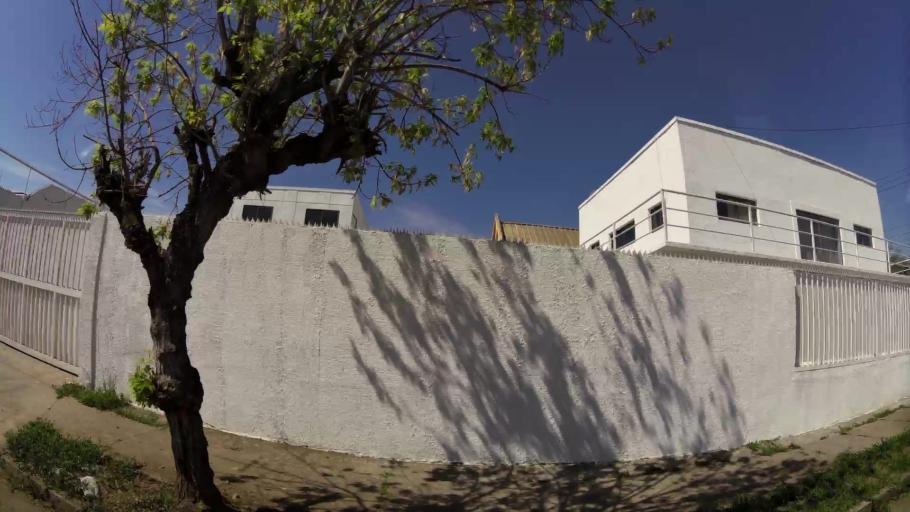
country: CL
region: Santiago Metropolitan
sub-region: Provincia de Santiago
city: La Pintana
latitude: -33.5294
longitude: -70.6604
